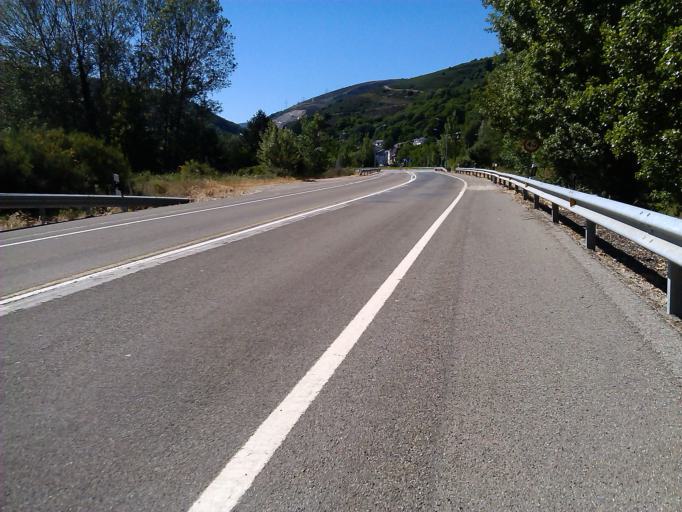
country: ES
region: Castille and Leon
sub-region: Provincia de Leon
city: Trabadelo
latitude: 42.6452
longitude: -6.8737
